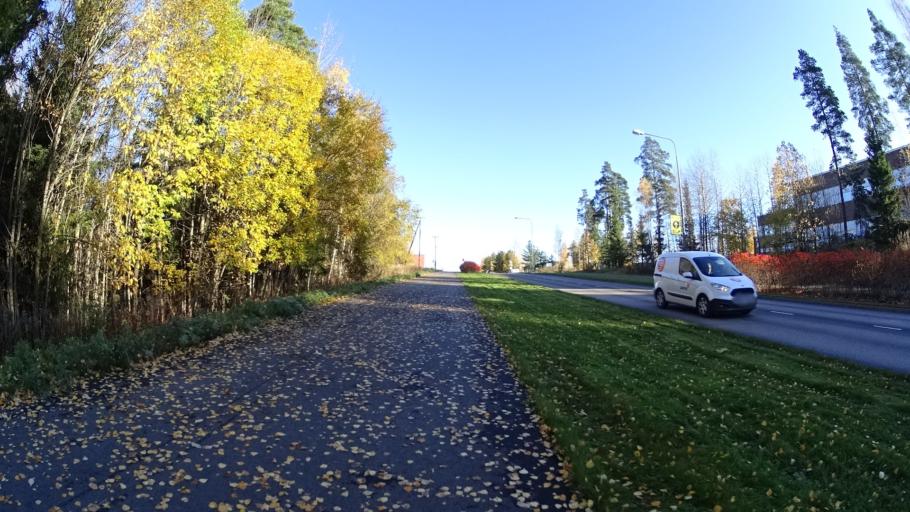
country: FI
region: Uusimaa
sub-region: Helsinki
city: Kauniainen
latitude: 60.2567
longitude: 24.7149
